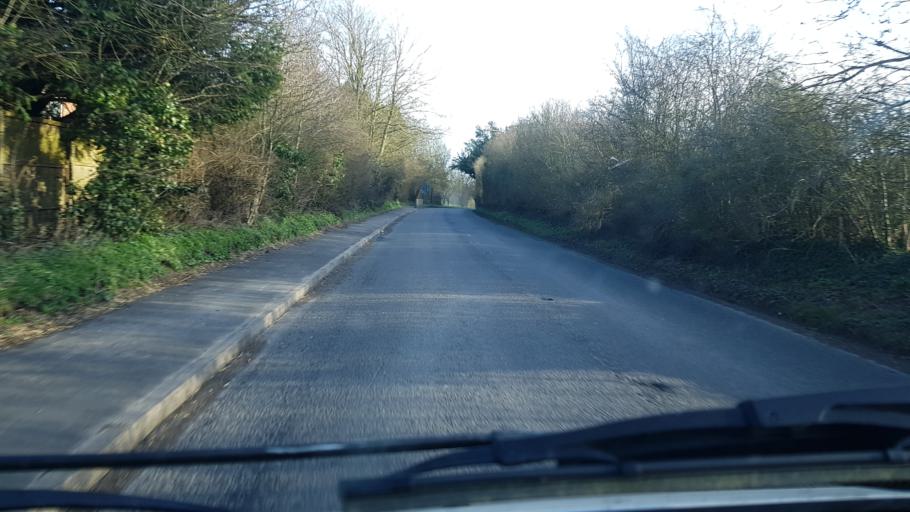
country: GB
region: England
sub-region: Wiltshire
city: Collingbourne Kingston
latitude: 51.3056
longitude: -1.6593
